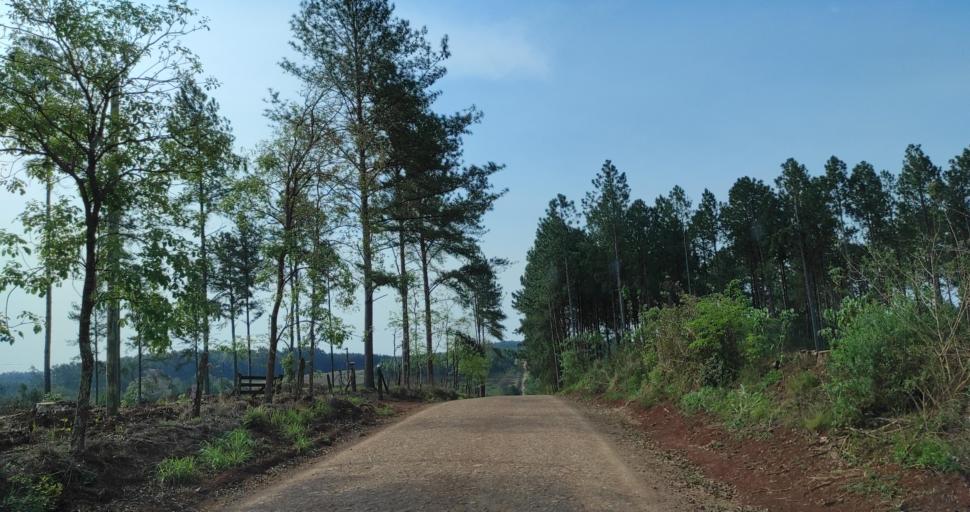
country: AR
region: Misiones
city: Garuhape
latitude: -26.8749
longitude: -55.0059
